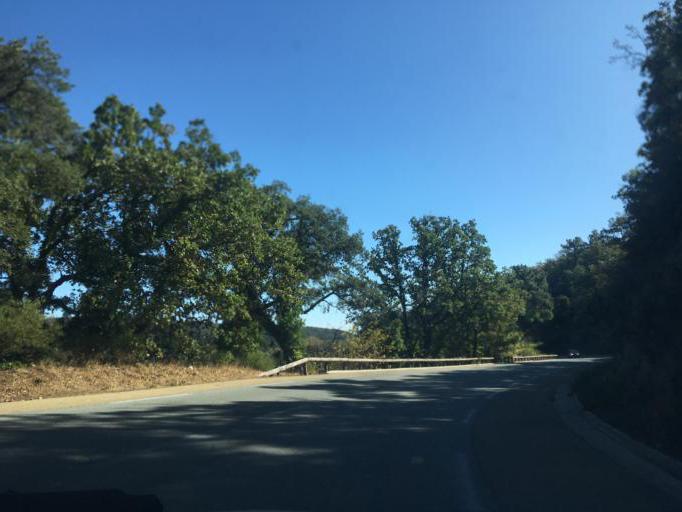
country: FR
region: Provence-Alpes-Cote d'Azur
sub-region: Departement du Var
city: La Garde-Freinet
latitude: 43.3030
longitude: 6.4838
